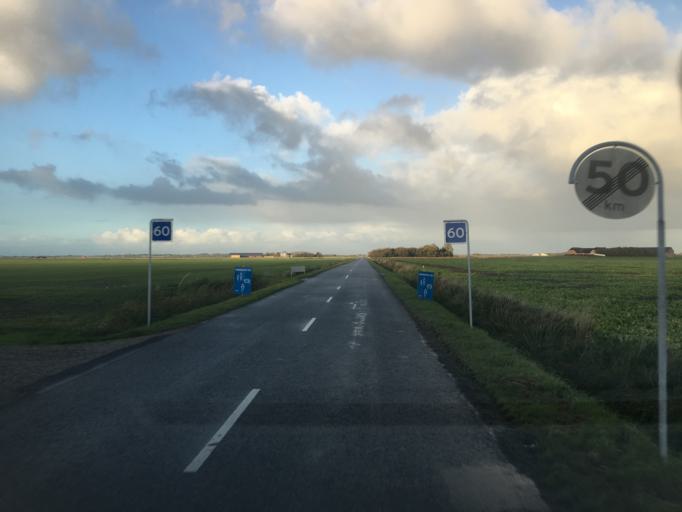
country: DE
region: Schleswig-Holstein
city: Neukirchen
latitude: 54.9034
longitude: 8.7547
